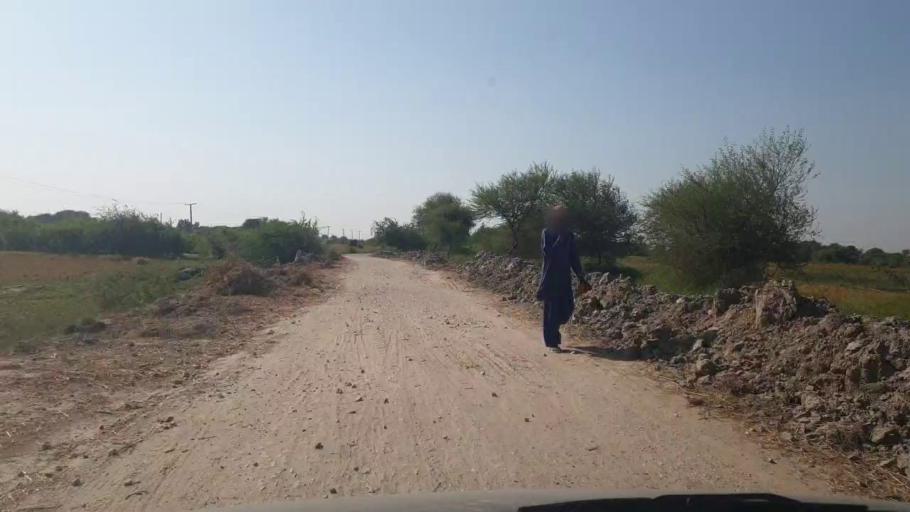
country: PK
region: Sindh
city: Badin
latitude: 24.5796
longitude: 68.7981
